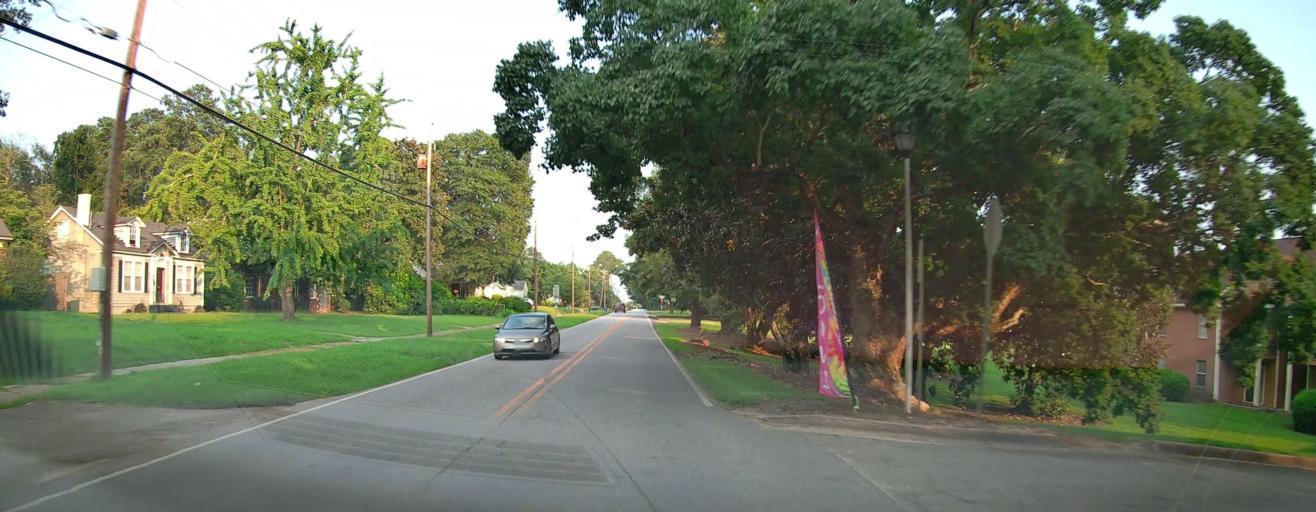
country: US
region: Georgia
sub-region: Bibb County
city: Macon
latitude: 32.8535
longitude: -83.6280
